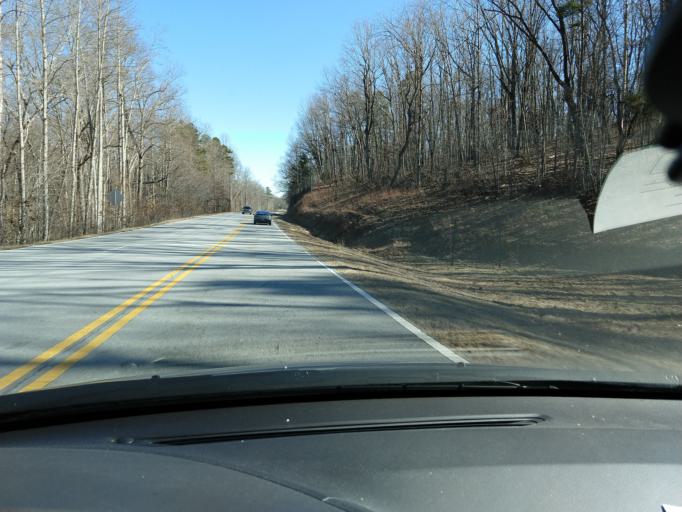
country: US
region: Georgia
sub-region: Stephens County
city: Toccoa
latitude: 34.6095
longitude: -83.3655
